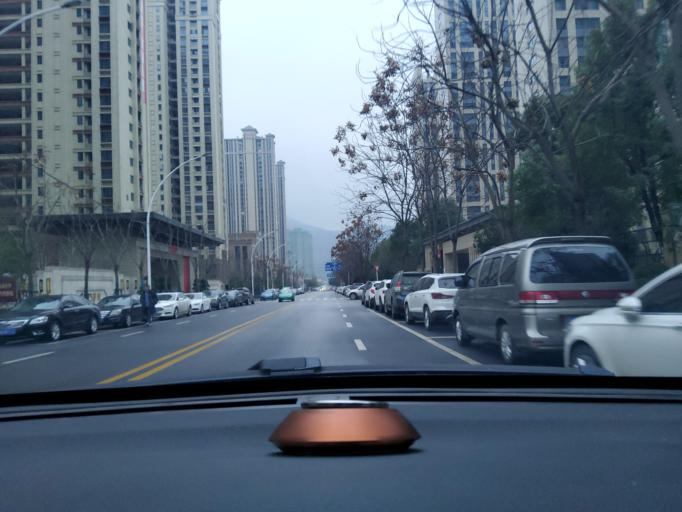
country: CN
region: Hubei
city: Tuanchengshan
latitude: 30.1978
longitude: 115.0094
